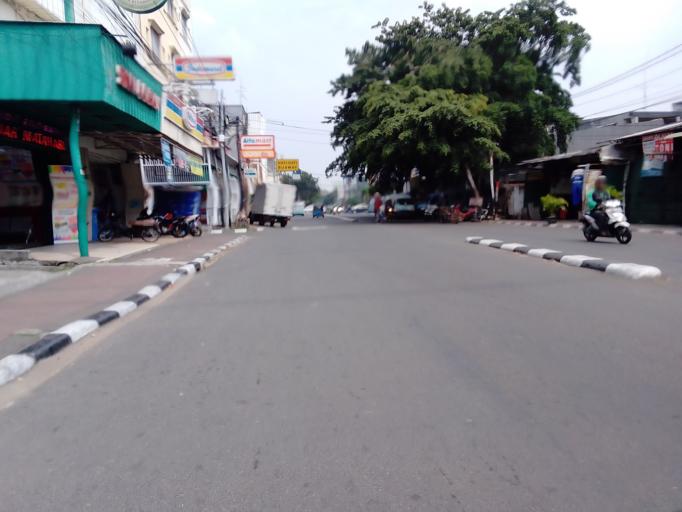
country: ID
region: Jakarta Raya
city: Jakarta
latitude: -6.1648
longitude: 106.8083
